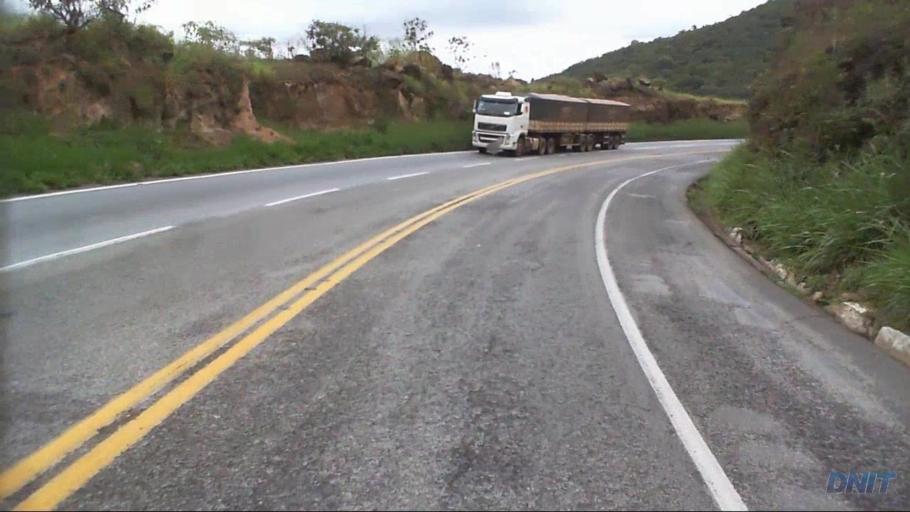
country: BR
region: Minas Gerais
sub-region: Joao Monlevade
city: Joao Monlevade
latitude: -19.8470
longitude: -43.3066
